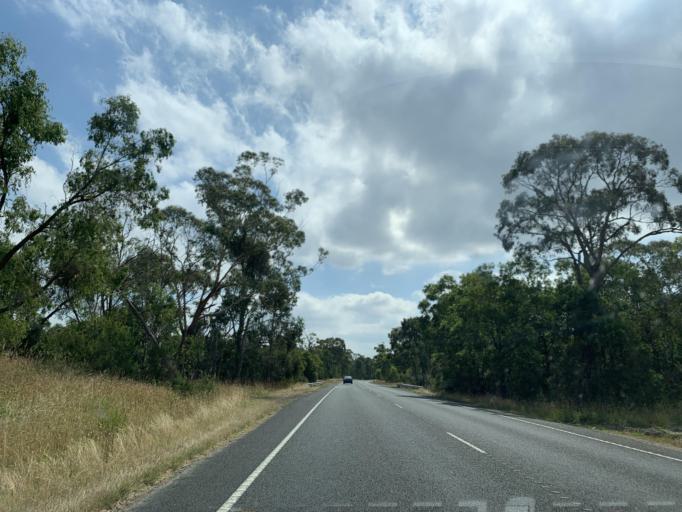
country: AU
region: Victoria
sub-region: Latrobe
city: Morwell
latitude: -38.2040
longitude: 146.4584
